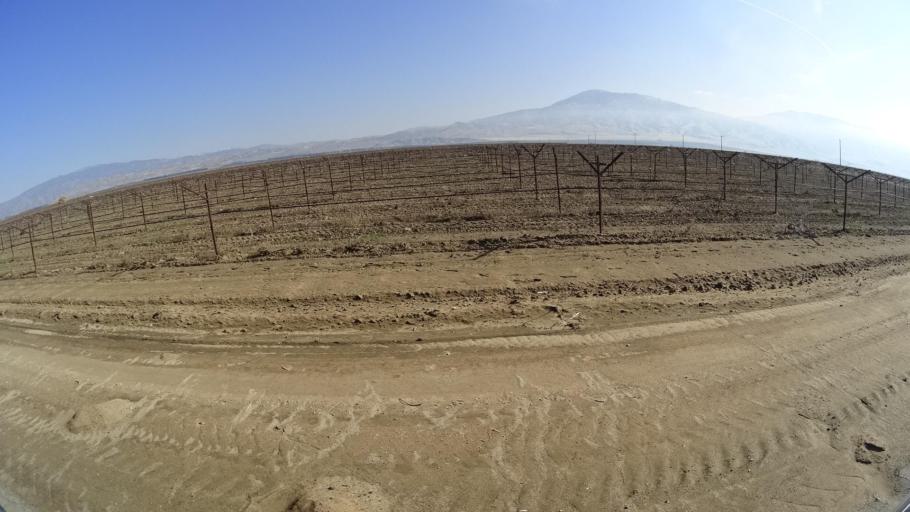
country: US
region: California
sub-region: Kern County
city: Arvin
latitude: 35.2541
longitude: -118.8069
